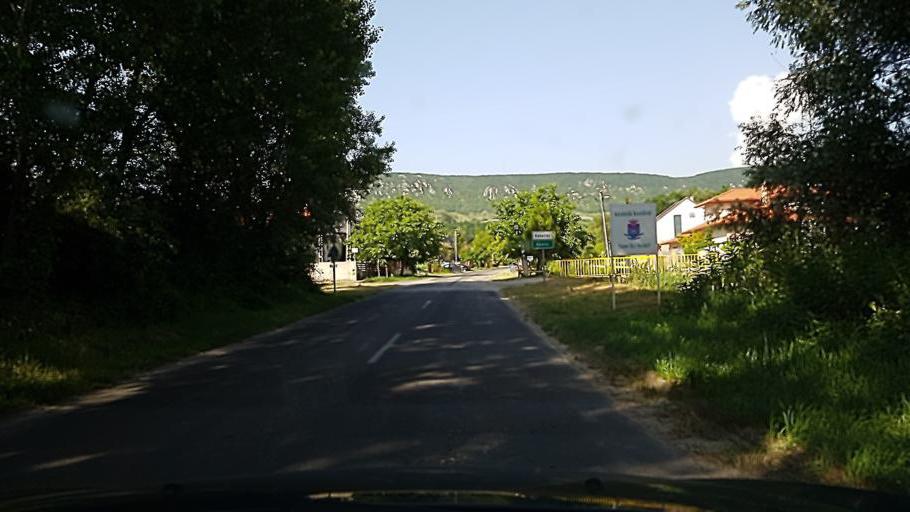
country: HU
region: Komarom-Esztergom
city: Kesztolc
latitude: 47.7080
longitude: 18.7851
